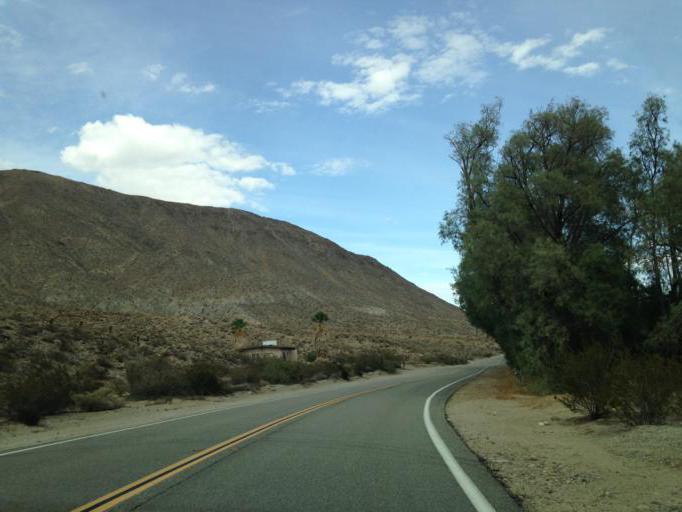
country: US
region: California
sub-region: San Diego County
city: Borrego Springs
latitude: 33.1379
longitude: -116.3776
